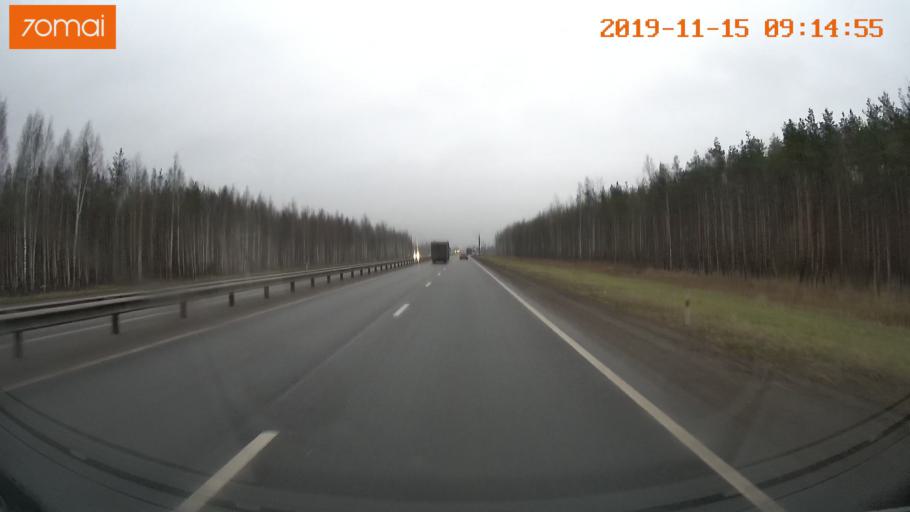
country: RU
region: Vologda
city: Tonshalovo
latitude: 59.2325
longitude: 37.9629
